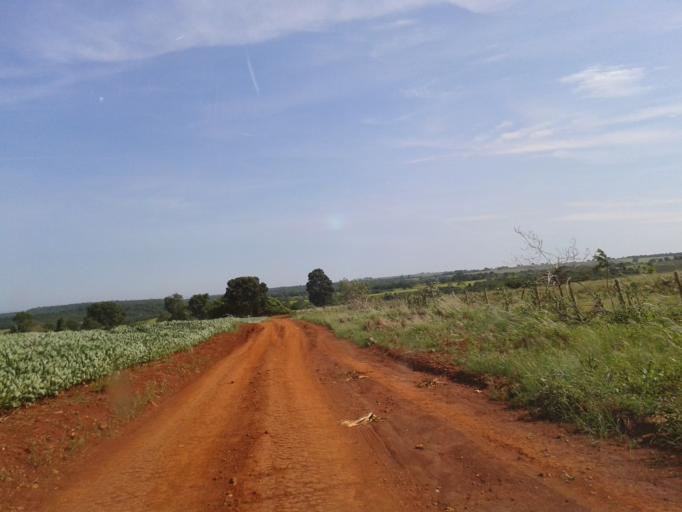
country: BR
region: Minas Gerais
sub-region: Centralina
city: Centralina
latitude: -18.7072
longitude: -49.2049
